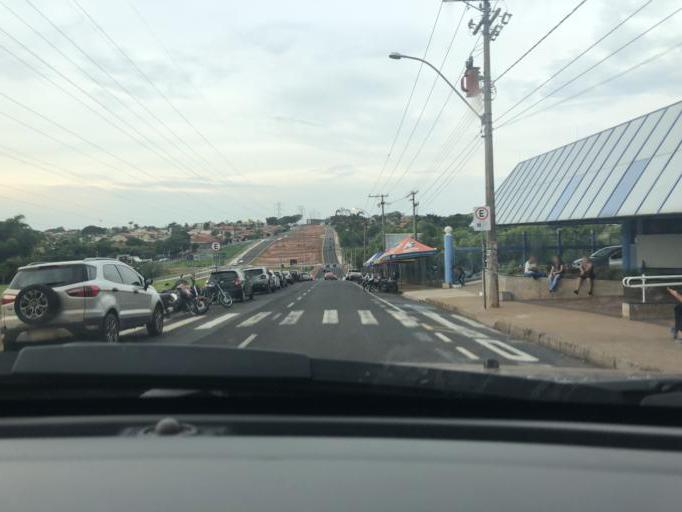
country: BR
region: Sao Paulo
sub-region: Sao Jose Do Rio Preto
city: Sao Jose do Rio Preto
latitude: -20.8425
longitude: -49.4132
